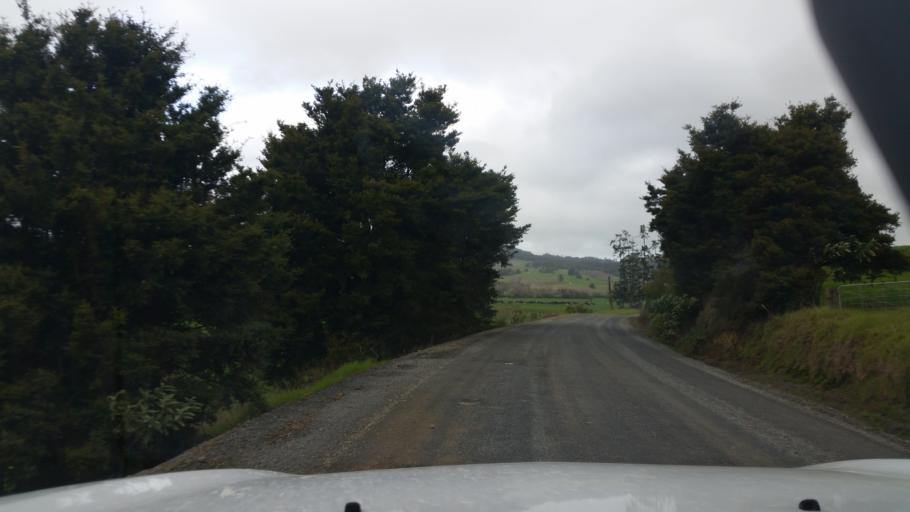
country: NZ
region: Northland
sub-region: Whangarei
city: Maungatapere
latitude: -35.6188
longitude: 174.1978
